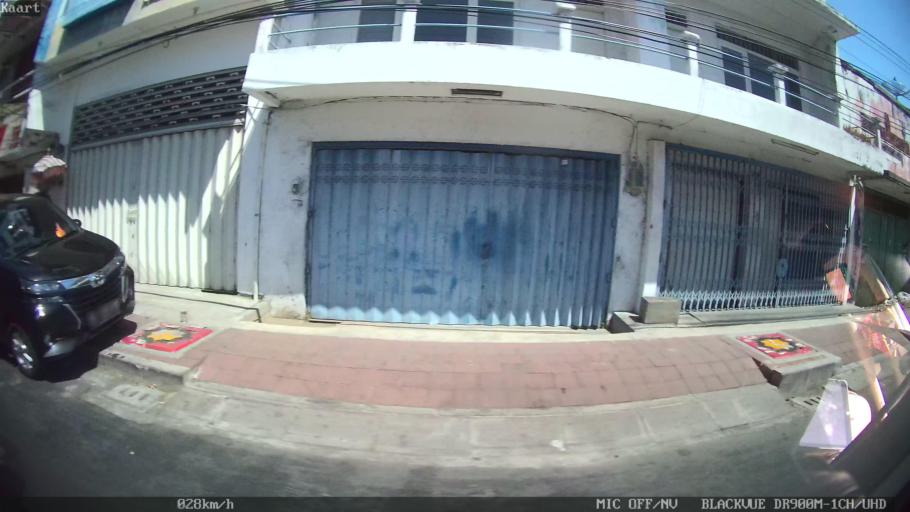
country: ID
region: Bali
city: Banjar Barunasari
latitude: -8.1036
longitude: 115.0918
